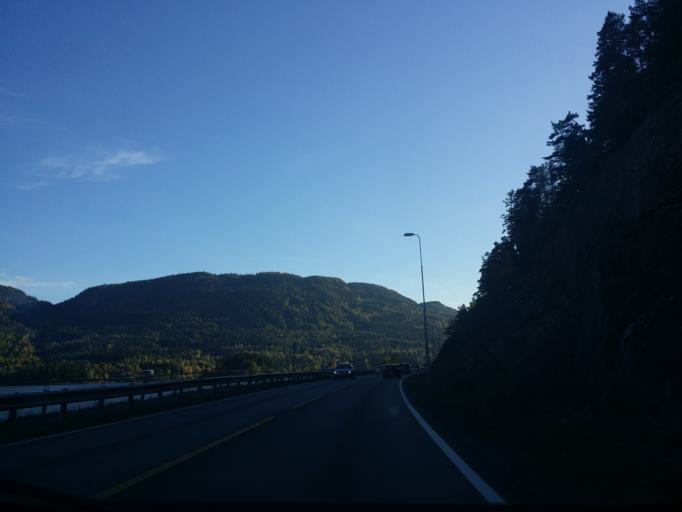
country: NO
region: Buskerud
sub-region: Hole
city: Vik
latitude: 60.0722
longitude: 10.3027
